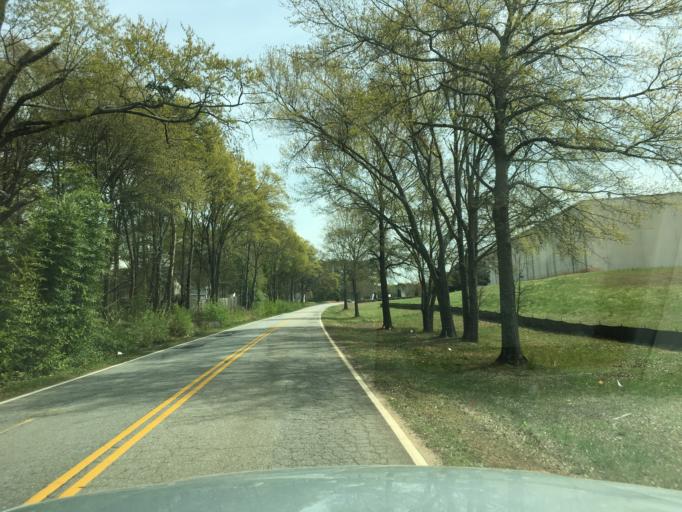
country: US
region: South Carolina
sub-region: Spartanburg County
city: Fairforest
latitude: 34.9504
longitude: -82.0083
